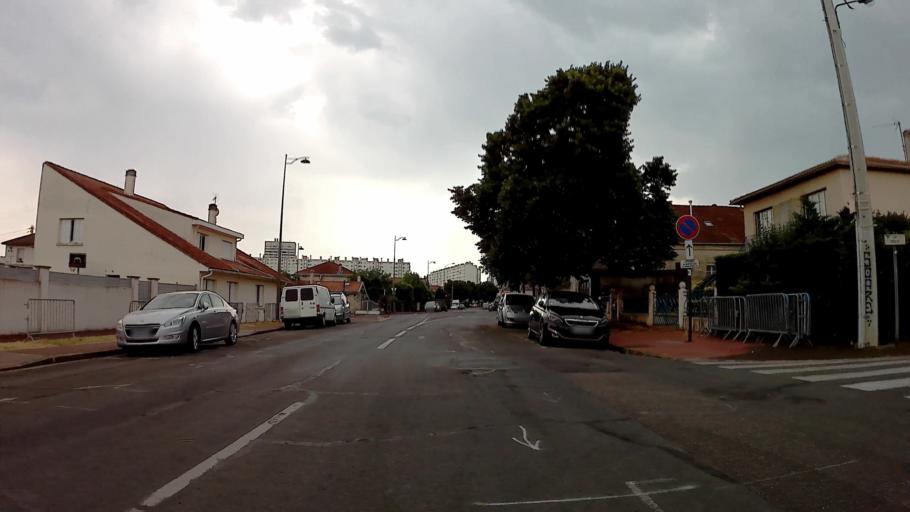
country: FR
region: Aquitaine
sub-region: Departement de la Gironde
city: Le Bouscat
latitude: 44.8650
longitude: -0.5883
